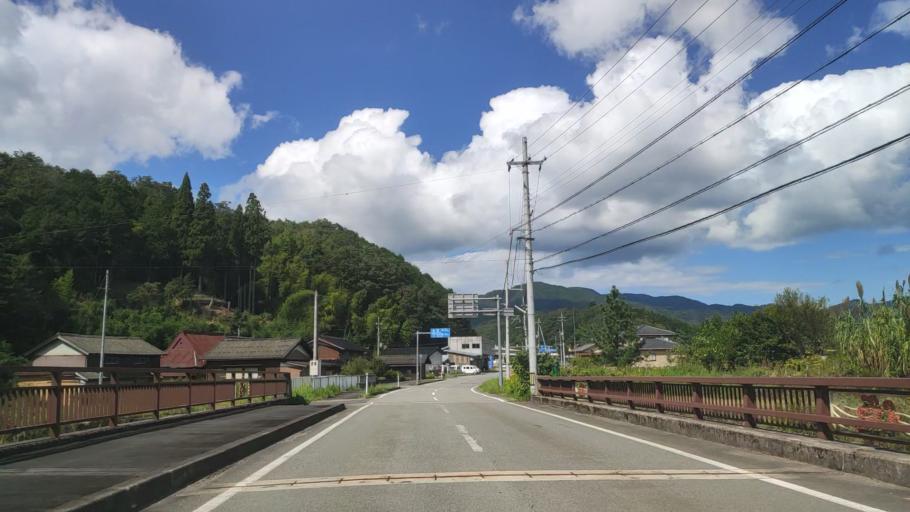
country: JP
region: Hyogo
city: Toyooka
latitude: 35.4916
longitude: 134.9930
